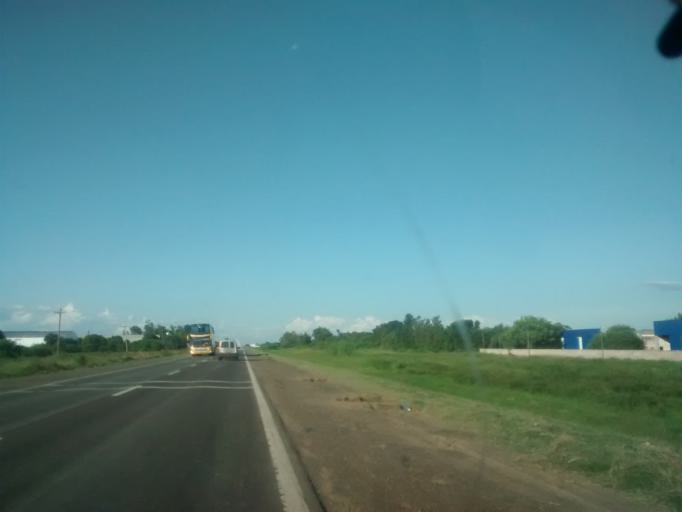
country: AR
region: Chaco
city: Fontana
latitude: -27.4732
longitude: -59.0537
